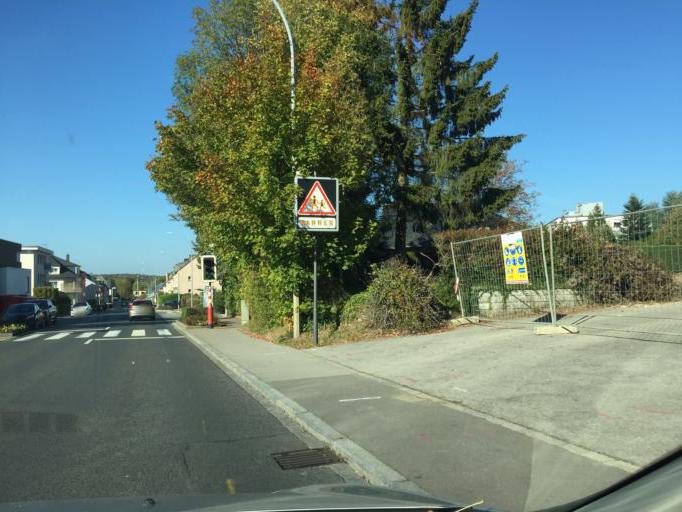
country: LU
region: Luxembourg
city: Bridel
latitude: 49.6568
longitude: 6.0829
